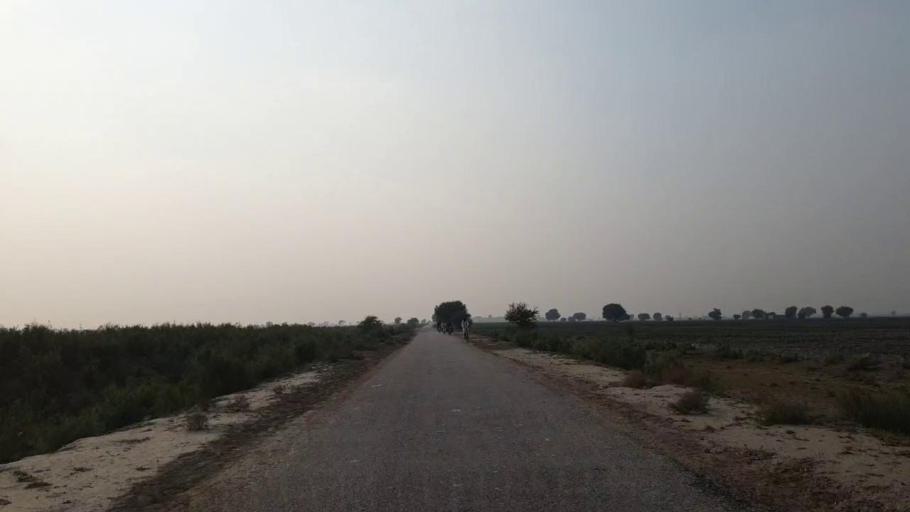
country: PK
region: Sindh
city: Bhan
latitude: 26.4886
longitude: 67.7211
